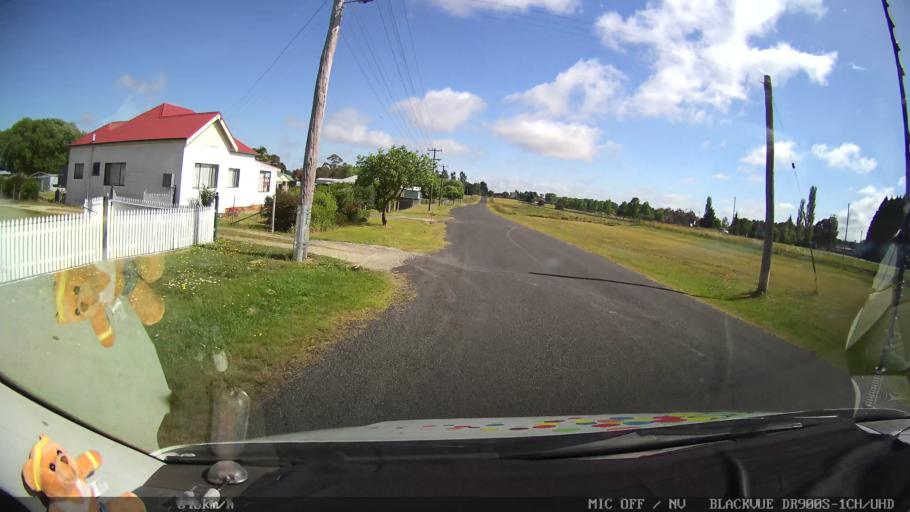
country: AU
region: New South Wales
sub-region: Guyra
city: Guyra
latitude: -30.2119
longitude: 151.6732
